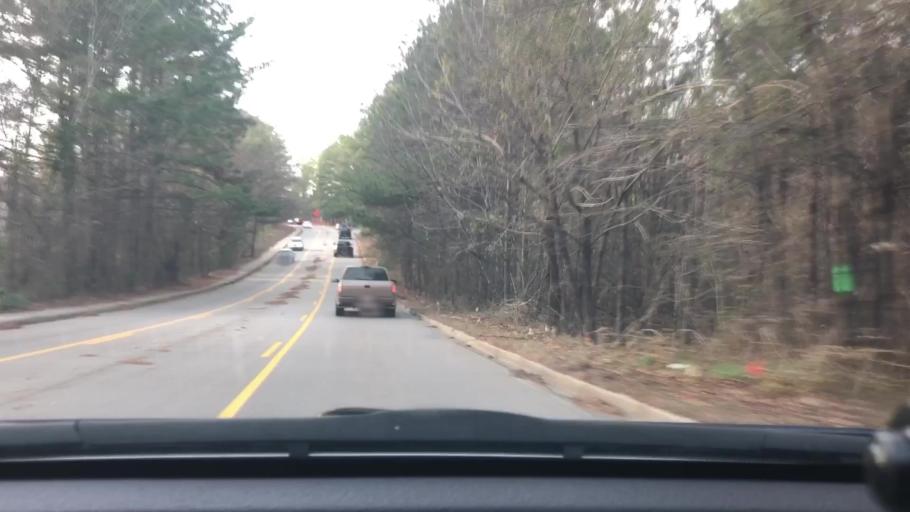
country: US
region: South Carolina
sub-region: Lexington County
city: Irmo
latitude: 34.0891
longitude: -81.1667
